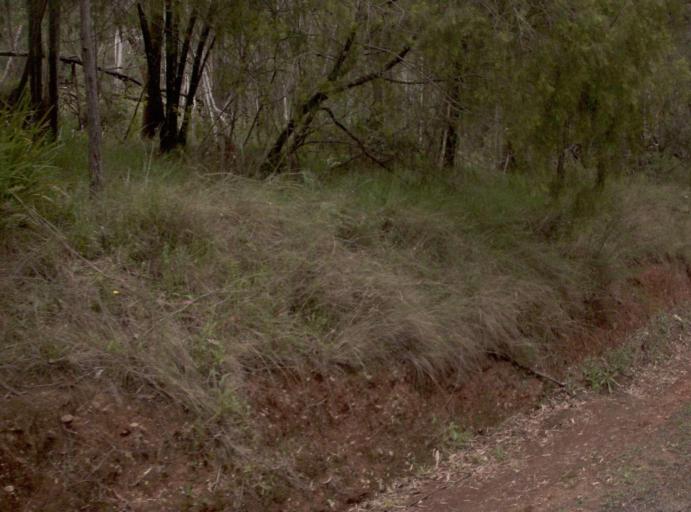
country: AU
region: New South Wales
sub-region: Bombala
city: Bombala
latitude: -37.4027
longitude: 149.1996
